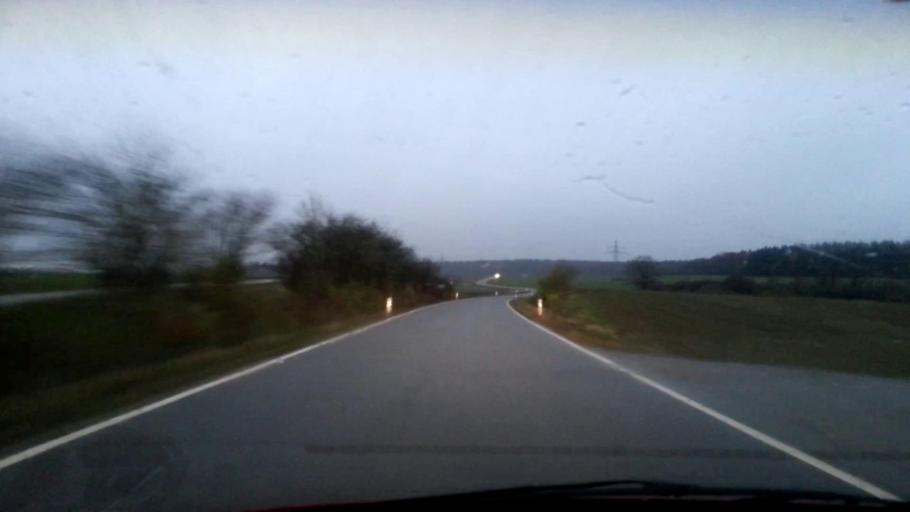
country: DE
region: Bavaria
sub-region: Upper Franconia
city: Konigsfeld
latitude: 49.9526
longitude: 11.1486
